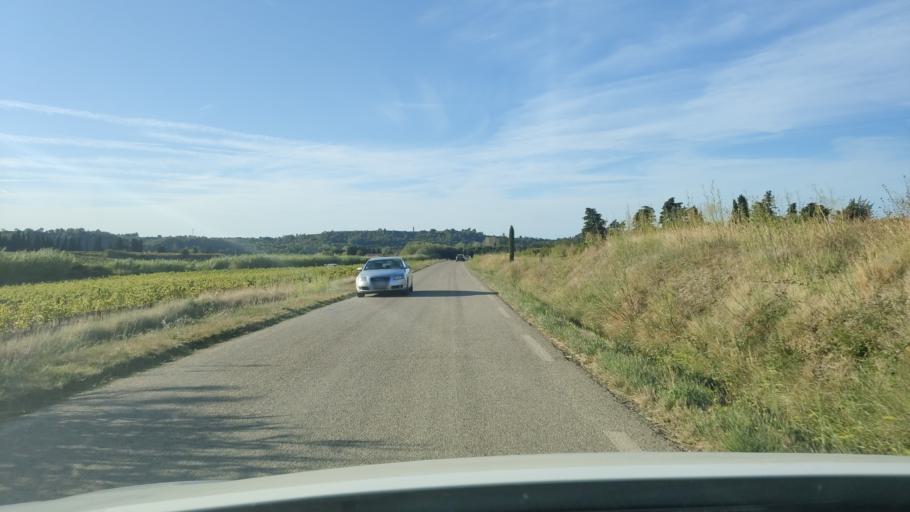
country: FR
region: Languedoc-Roussillon
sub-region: Departement du Gard
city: Saze
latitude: 43.9397
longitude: 4.6526
